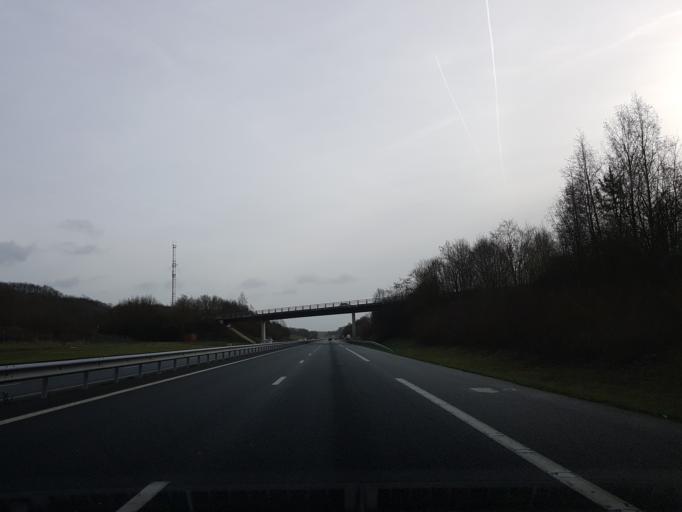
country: FR
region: Bourgogne
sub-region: Departement de l'Yonne
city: Soucy
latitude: 48.2689
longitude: 3.2936
